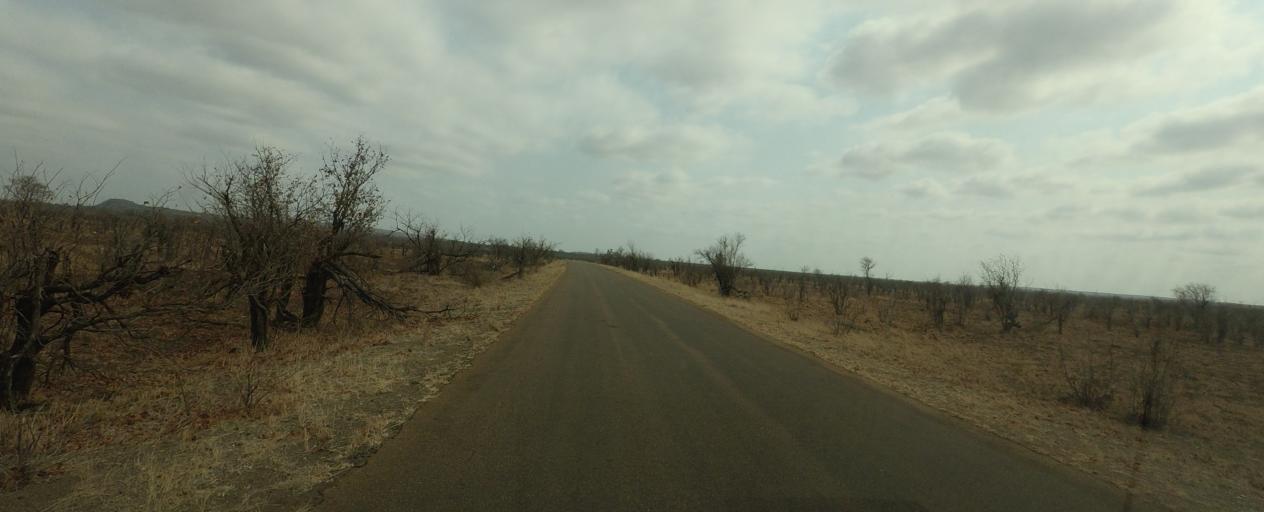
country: ZA
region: Limpopo
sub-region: Vhembe District Municipality
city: Mutale
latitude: -22.6317
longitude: 31.1802
